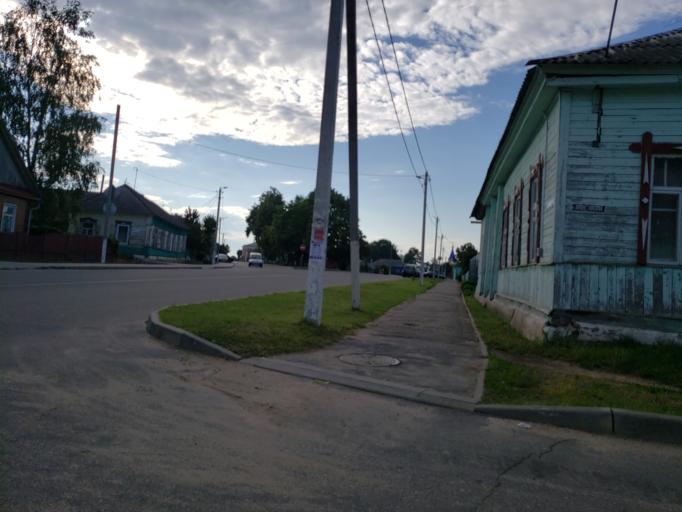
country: BY
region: Minsk
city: Chervyen'
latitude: 53.7094
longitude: 28.4278
